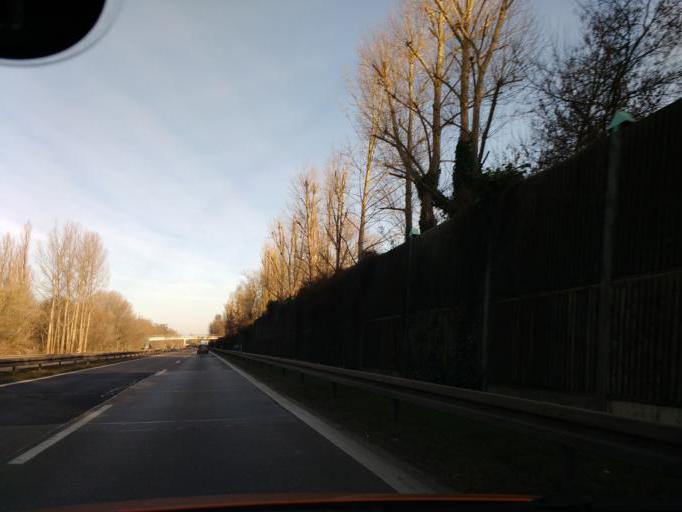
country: DE
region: Berlin
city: Blankenburg
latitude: 52.5982
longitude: 13.4459
